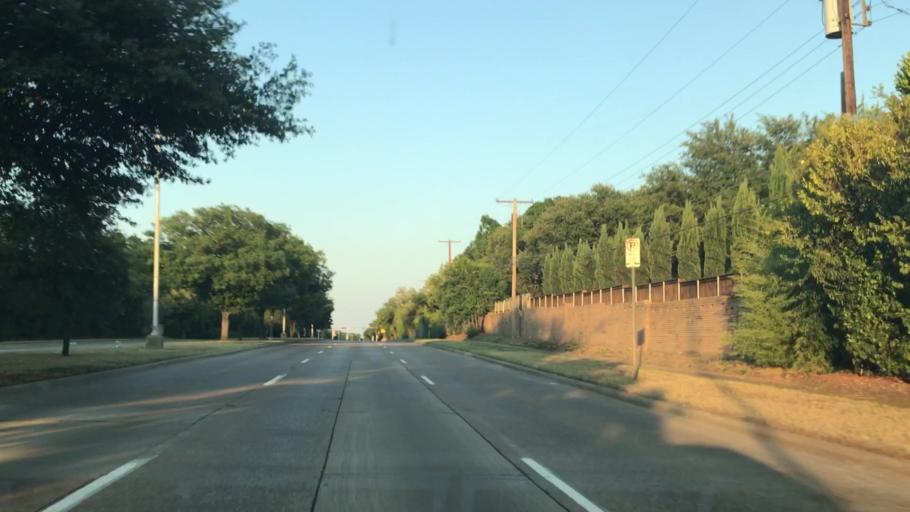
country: US
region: Texas
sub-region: Dallas County
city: Addison
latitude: 32.9095
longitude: -96.8335
